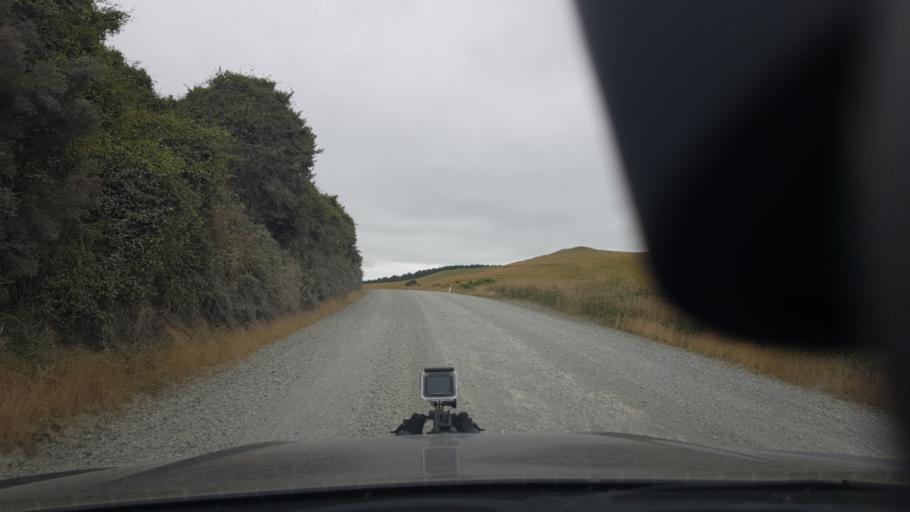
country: NZ
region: Otago
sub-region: Clutha District
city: Papatowai
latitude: -46.3324
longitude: 169.4066
